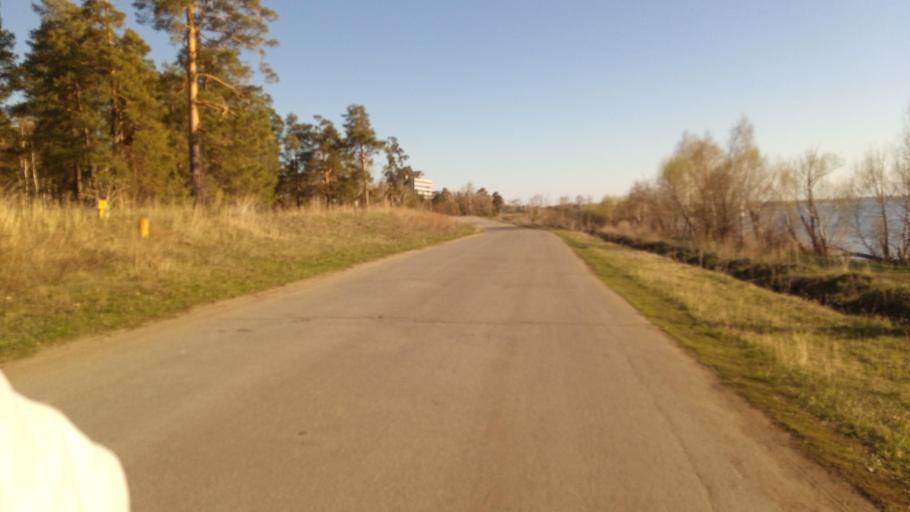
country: RU
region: Chelyabinsk
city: Novosineglazovskiy
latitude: 55.1286
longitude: 61.3282
